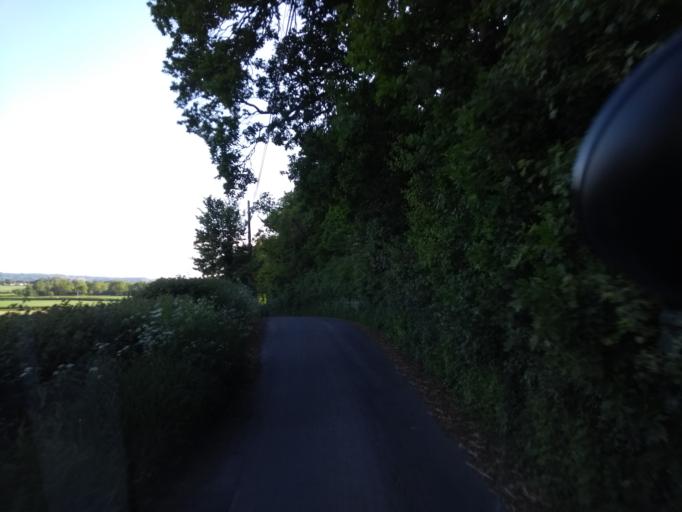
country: GB
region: England
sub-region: Somerset
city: Creech Saint Michael
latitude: 51.0024
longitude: -3.0521
